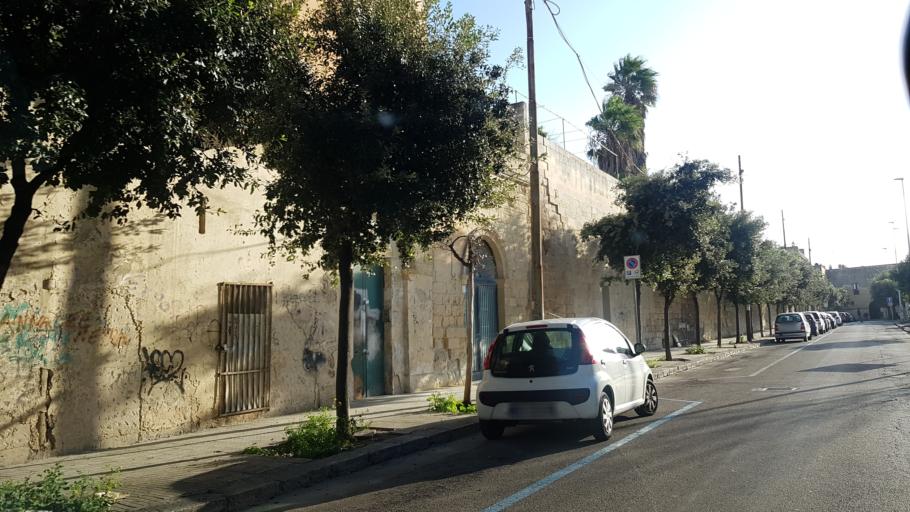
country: IT
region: Apulia
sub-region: Provincia di Lecce
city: Lecce
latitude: 40.3542
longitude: 18.1666
